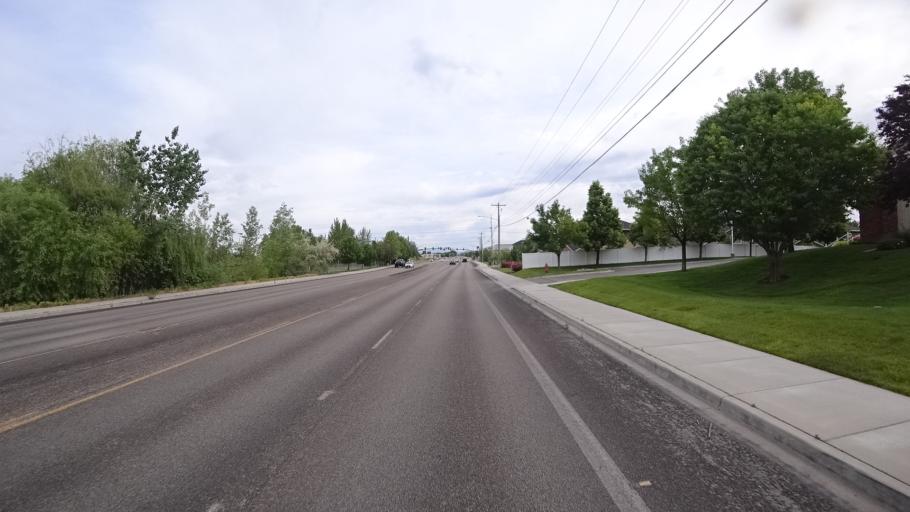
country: US
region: Idaho
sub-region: Ada County
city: Meridian
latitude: 43.6032
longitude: -116.3745
